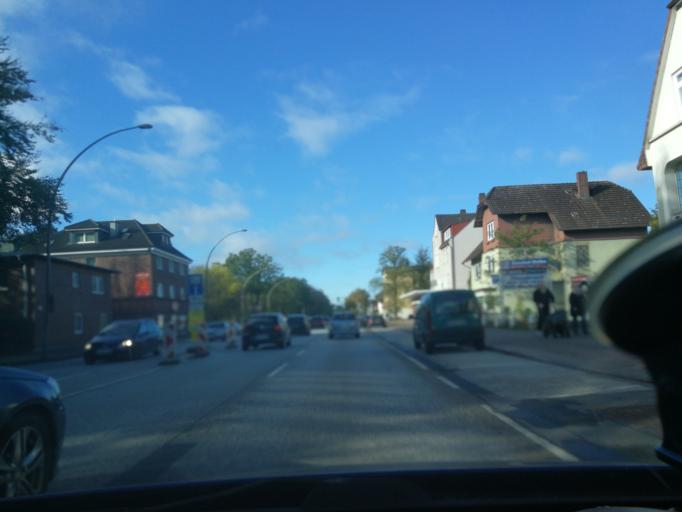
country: DE
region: Hamburg
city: Altona
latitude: 53.4719
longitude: 9.8907
